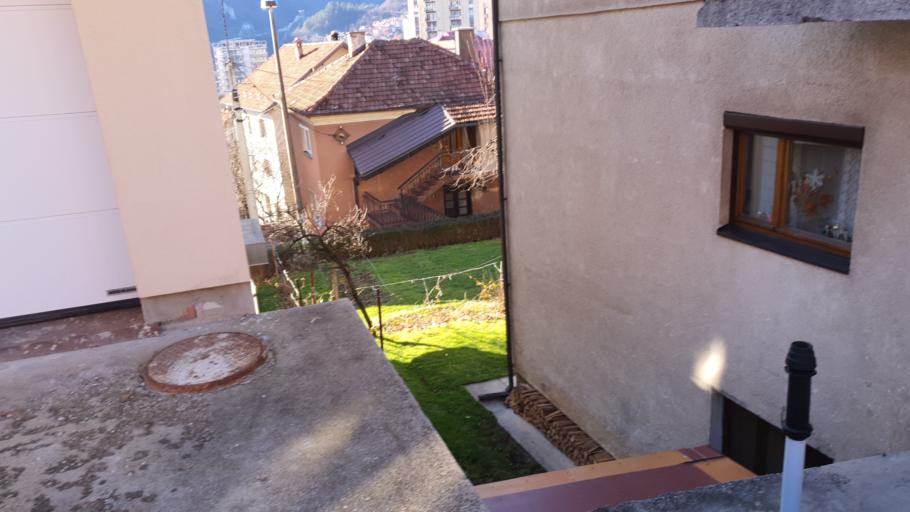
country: RS
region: Central Serbia
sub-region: Zlatiborski Okrug
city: Uzice
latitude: 43.8589
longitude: 19.8444
